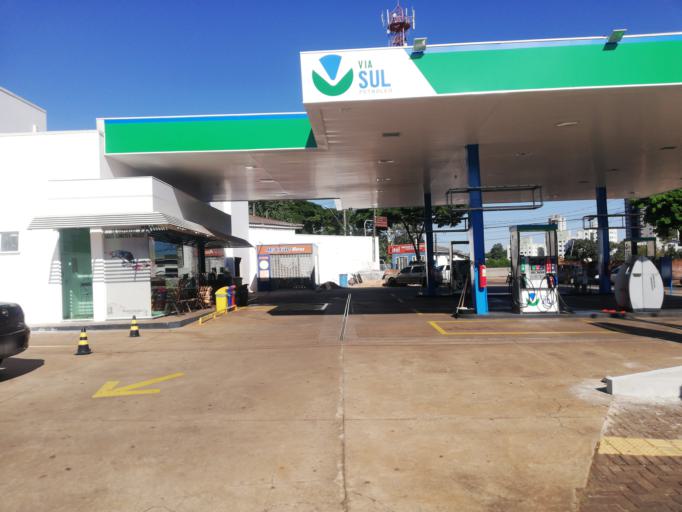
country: BR
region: Parana
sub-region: Foz Do Iguacu
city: Foz do Iguacu
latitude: -25.5478
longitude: -54.5781
